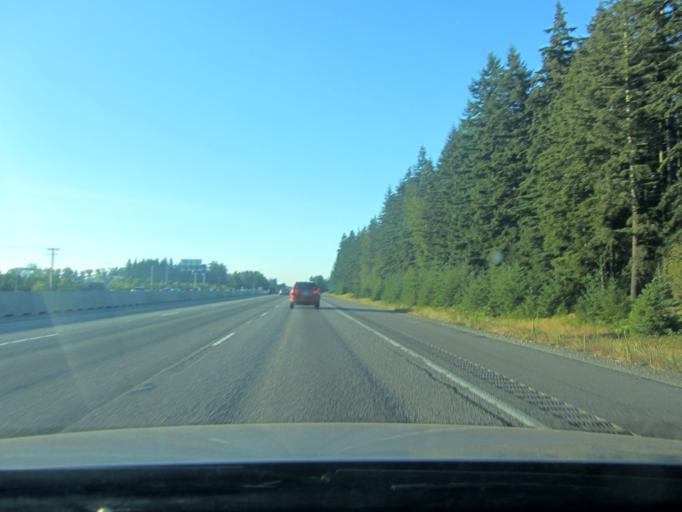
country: US
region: Washington
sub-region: Snohomish County
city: Marysville
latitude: 48.0896
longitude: -122.1846
